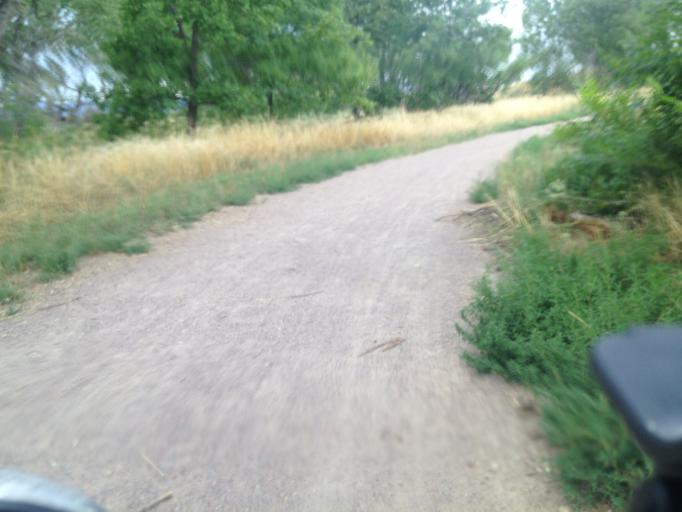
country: US
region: Colorado
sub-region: Boulder County
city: Louisville
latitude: 39.9806
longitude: -105.1231
